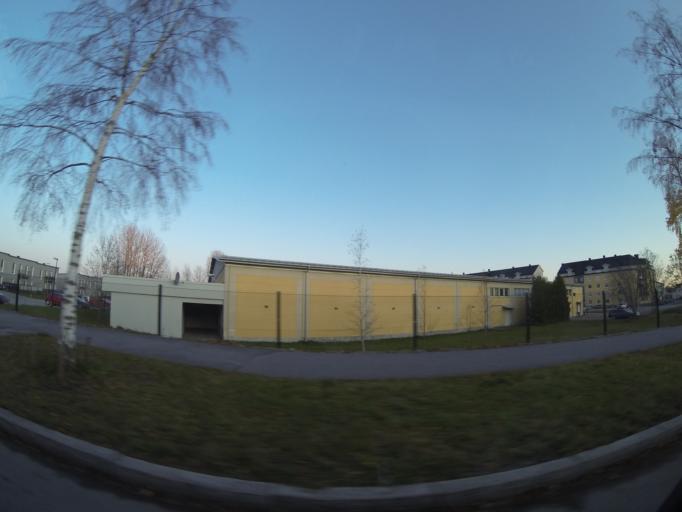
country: SE
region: OErebro
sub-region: Orebro Kommun
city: Orebro
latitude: 59.2839
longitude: 15.2375
